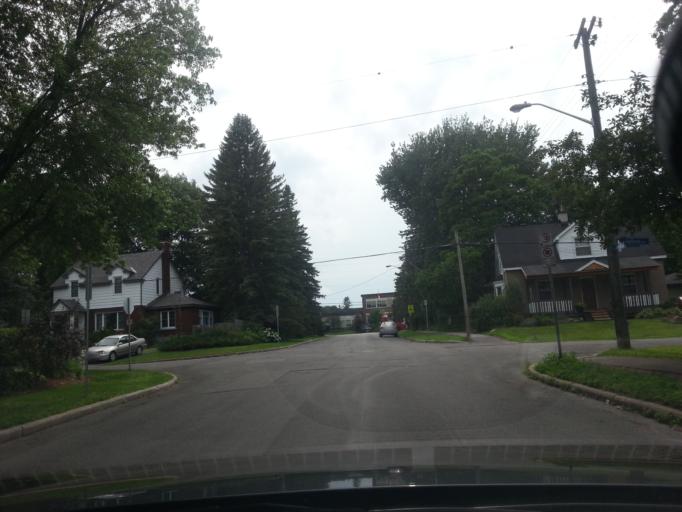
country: CA
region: Ontario
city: Ottawa
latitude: 45.3836
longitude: -75.7566
